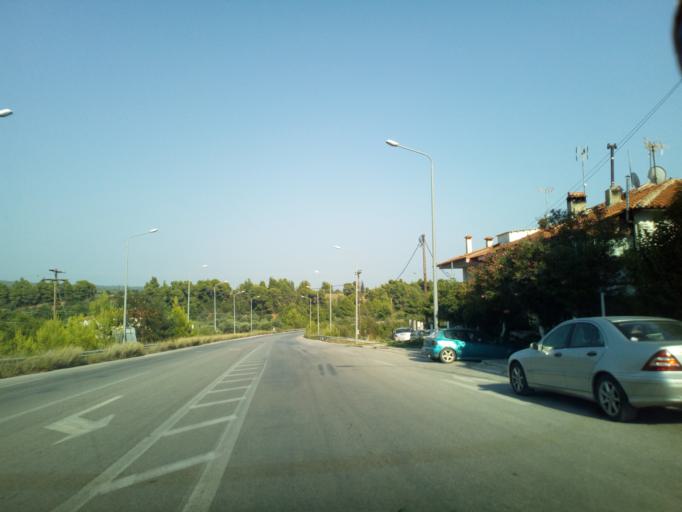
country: GR
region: Central Macedonia
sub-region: Nomos Chalkidikis
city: Nikiti
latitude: 40.2326
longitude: 23.6035
